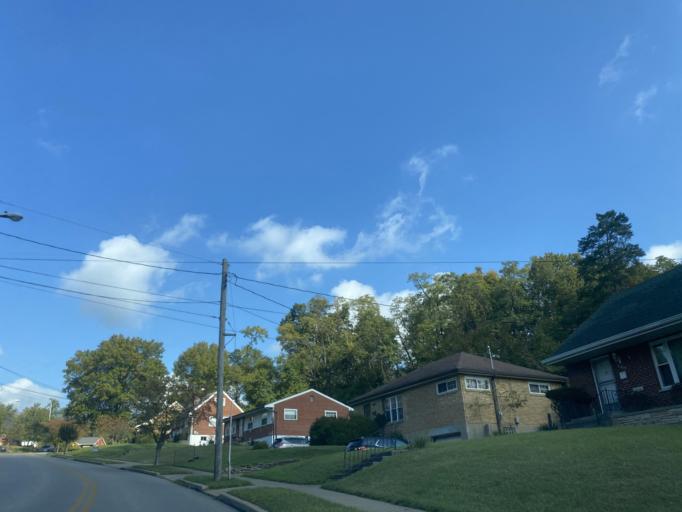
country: US
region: Kentucky
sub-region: Campbell County
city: Fort Thomas
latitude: 39.0915
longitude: -84.4570
